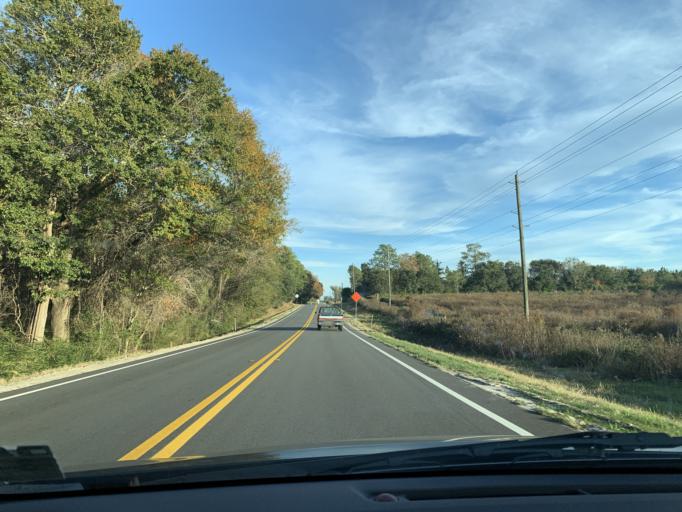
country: US
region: Georgia
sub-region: Irwin County
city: Ocilla
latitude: 31.5940
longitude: -83.1086
